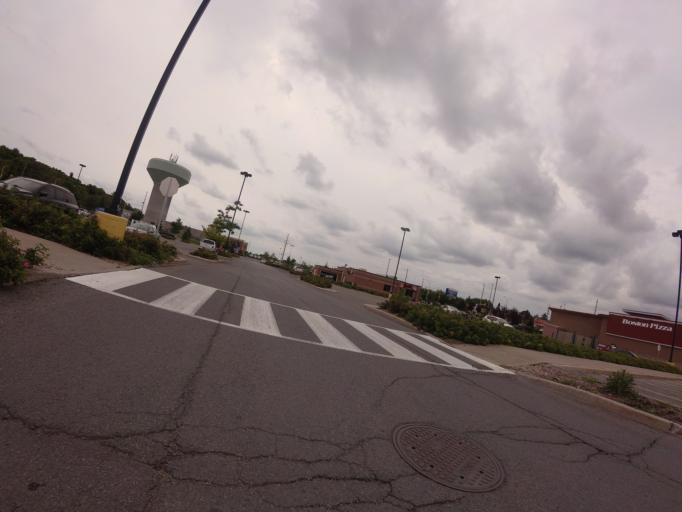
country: CA
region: Ontario
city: Ottawa
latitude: 45.4527
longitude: -75.5098
